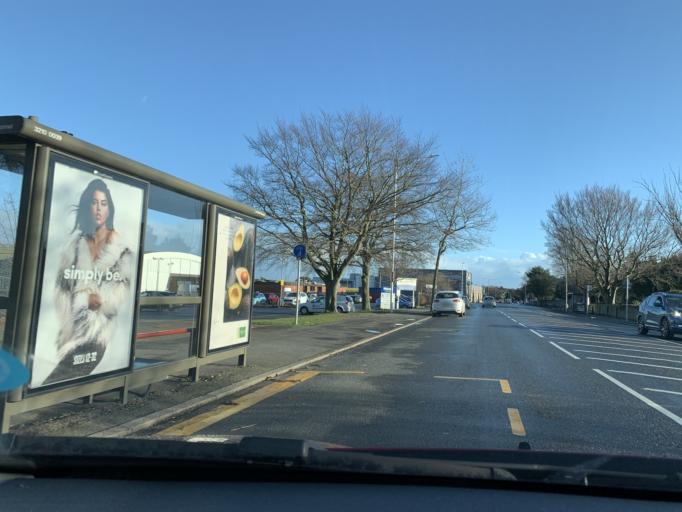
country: GB
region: England
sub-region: Kent
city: Folkestone
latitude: 51.0855
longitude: 1.1580
